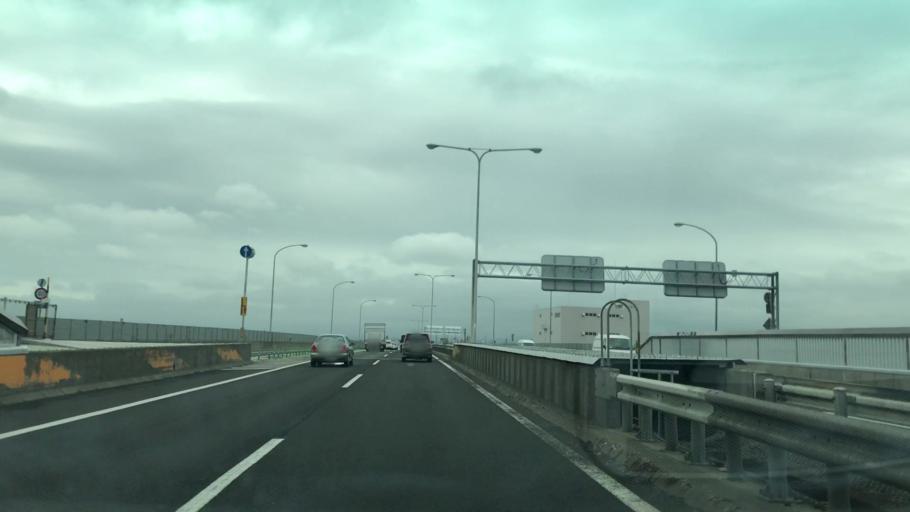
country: JP
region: Hokkaido
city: Sapporo
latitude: 43.0749
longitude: 141.4211
